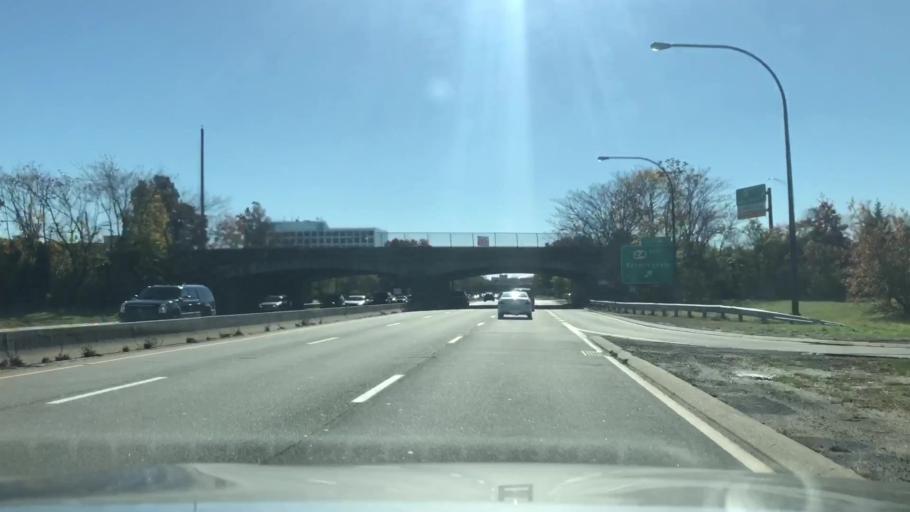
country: US
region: New York
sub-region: Nassau County
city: East Garden City
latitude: 40.7231
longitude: -73.5806
